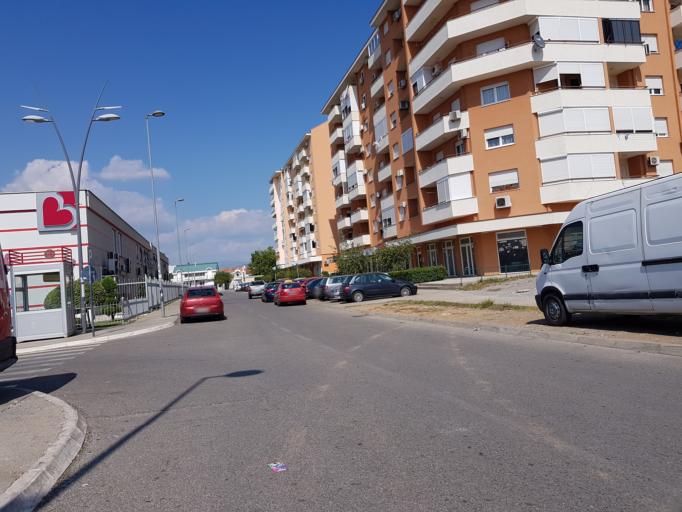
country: ME
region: Podgorica
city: Podgorica
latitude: 42.4284
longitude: 19.2722
